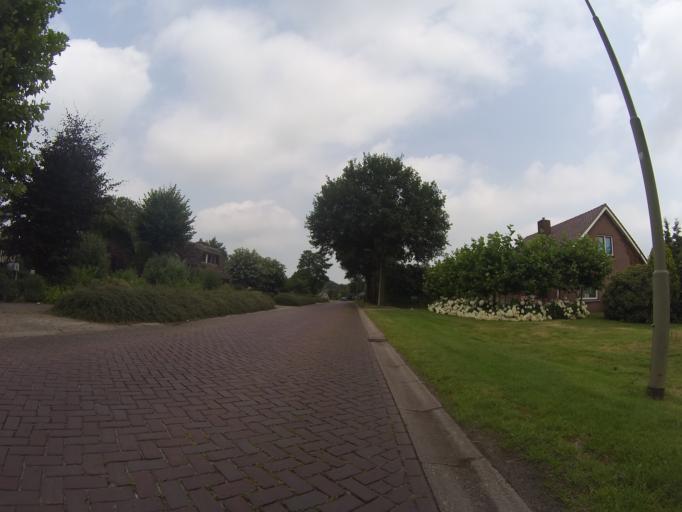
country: NL
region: Drenthe
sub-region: Gemeente Emmen
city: Emmen
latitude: 52.8226
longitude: 6.9173
